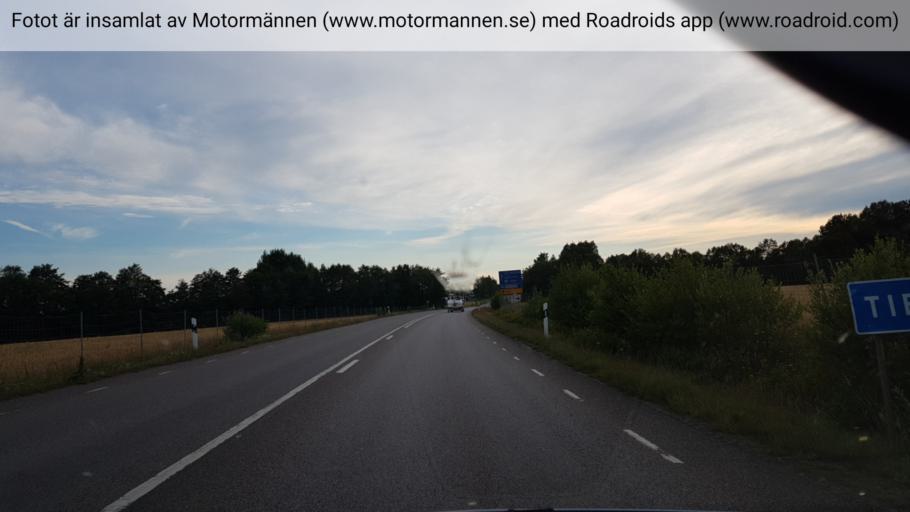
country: SE
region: Vaestra Goetaland
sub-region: Tibro Kommun
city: Tibro
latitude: 58.4345
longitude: 14.1676
